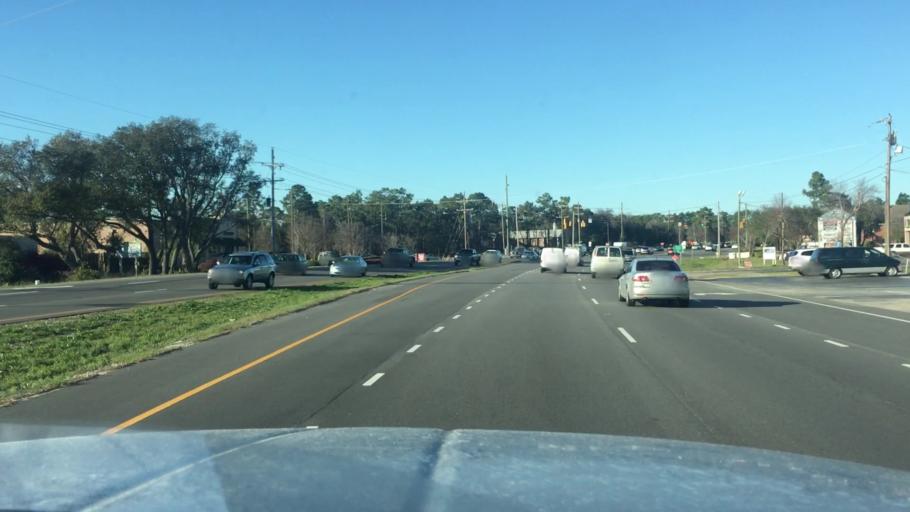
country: US
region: North Carolina
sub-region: New Hanover County
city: Myrtle Grove
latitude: 34.1243
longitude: -77.8999
